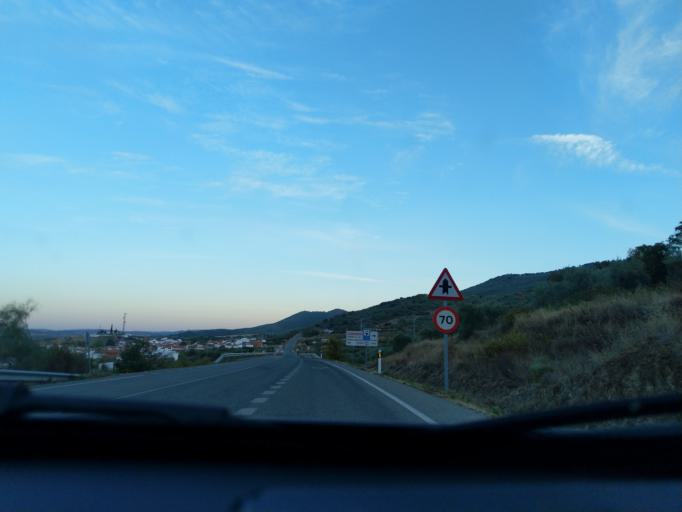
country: ES
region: Extremadura
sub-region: Provincia de Badajoz
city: Reina
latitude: 38.1543
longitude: -5.9041
